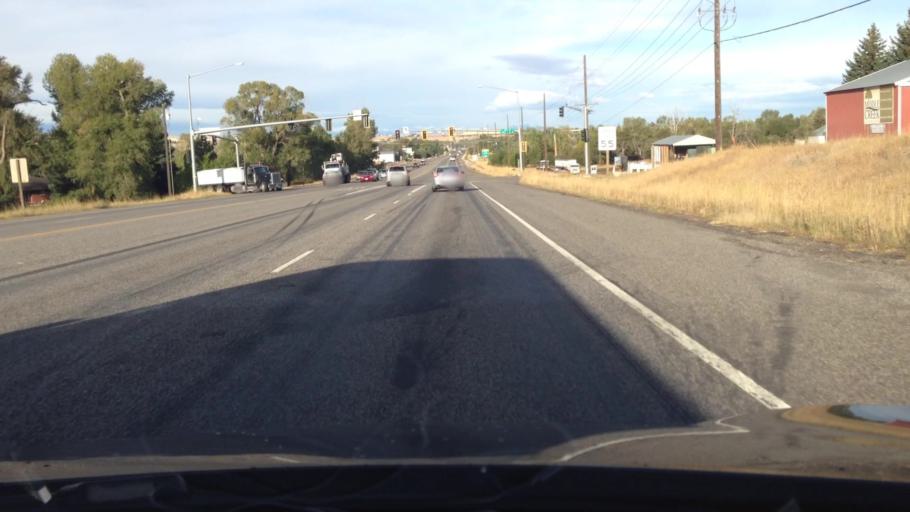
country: US
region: Montana
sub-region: Gallatin County
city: Four Corners
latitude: 45.6711
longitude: -111.1633
